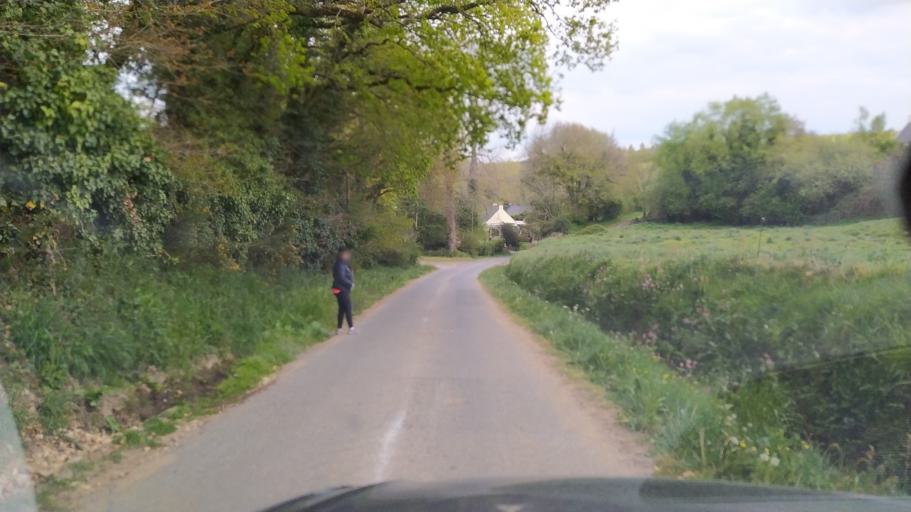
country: FR
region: Brittany
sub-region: Departement du Finistere
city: Bodilis
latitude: 48.5007
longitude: -4.1031
